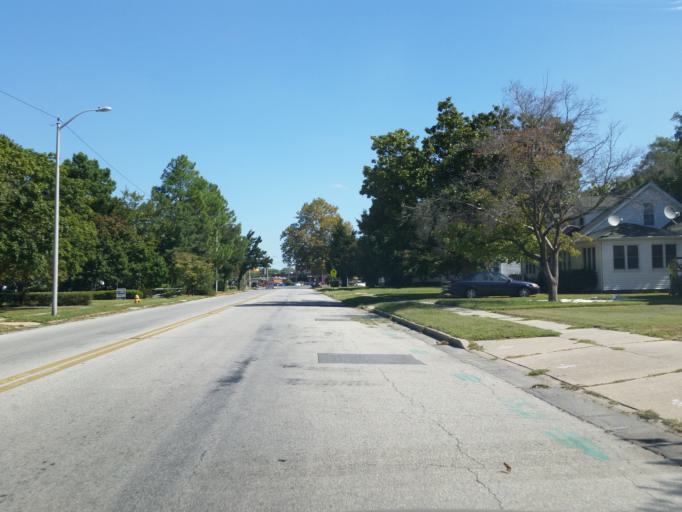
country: US
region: Maryland
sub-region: Wicomico County
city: Salisbury
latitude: 38.3716
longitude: -75.5781
